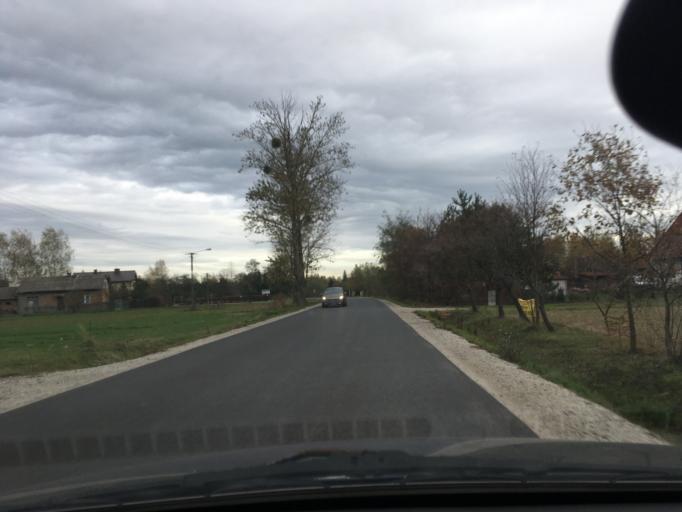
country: PL
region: Lodz Voivodeship
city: Zabia Wola
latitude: 52.0122
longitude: 20.7138
